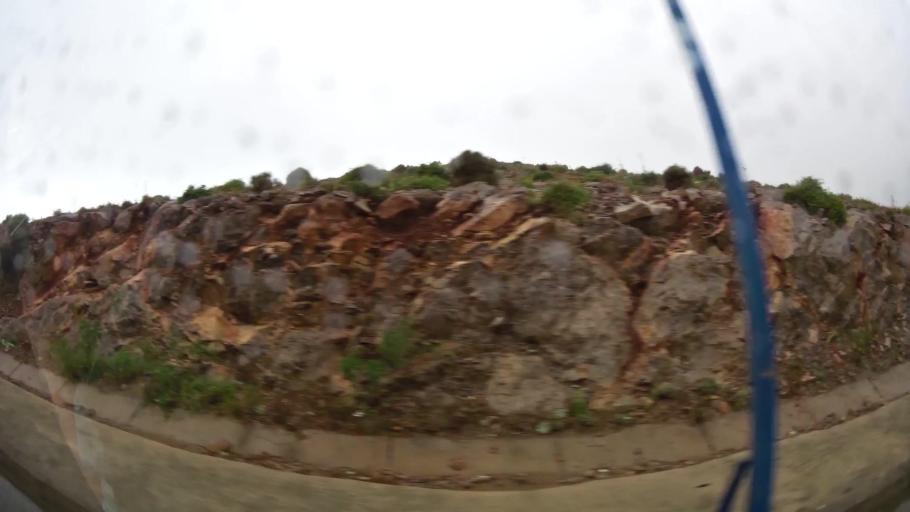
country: MA
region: Taza-Al Hoceima-Taounate
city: Al Hoceima
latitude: 35.2573
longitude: -3.9361
